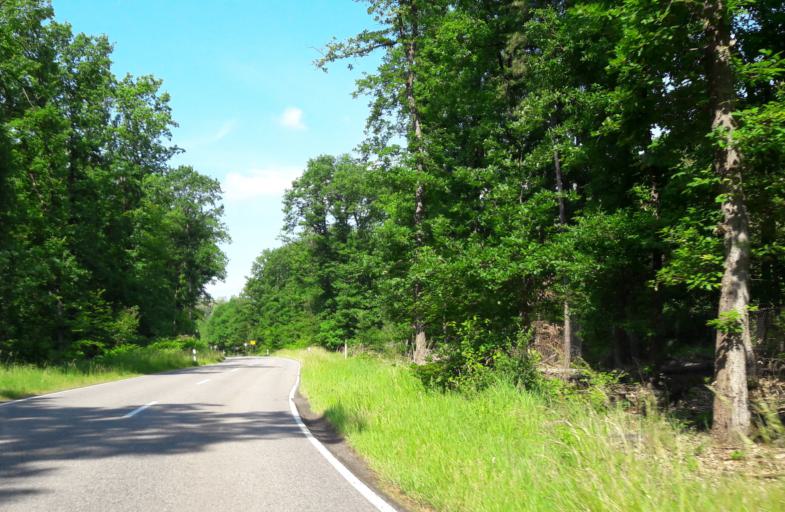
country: DE
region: Saarland
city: Ensdorf
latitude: 49.3149
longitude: 6.7901
